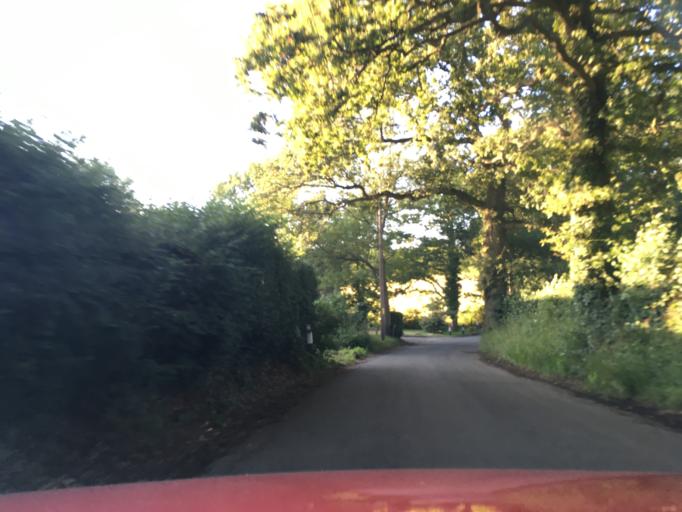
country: GB
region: England
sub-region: Hampshire
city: Tadley
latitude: 51.4204
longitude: -1.1634
